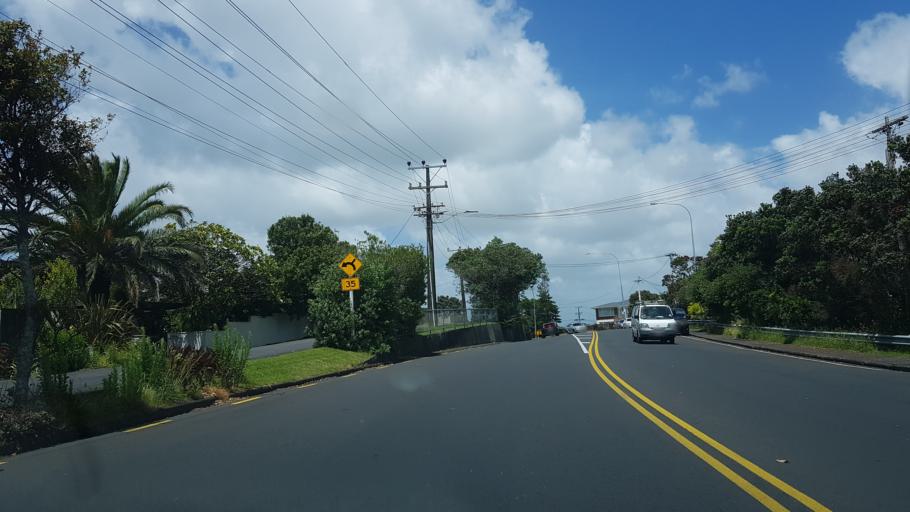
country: NZ
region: Auckland
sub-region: Auckland
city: North Shore
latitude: -36.7884
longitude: 174.7213
